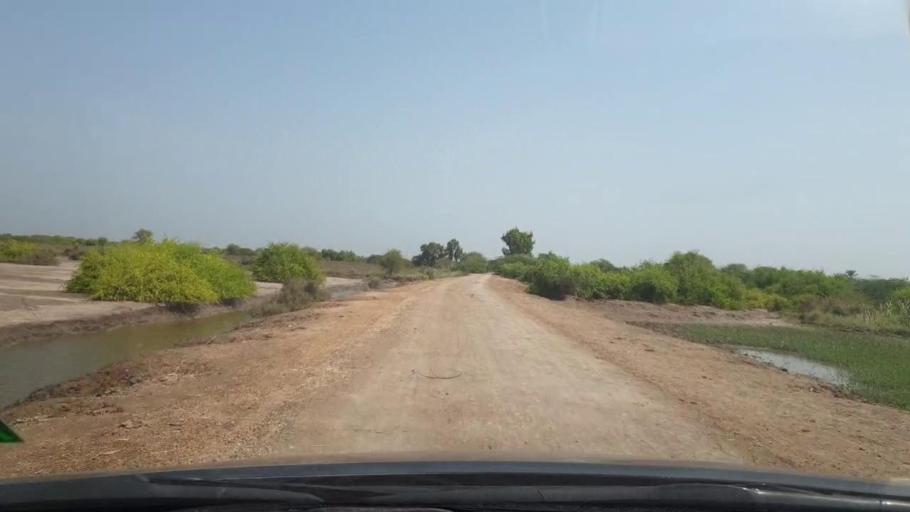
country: PK
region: Sindh
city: Tando Bago
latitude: 24.7997
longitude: 69.1038
